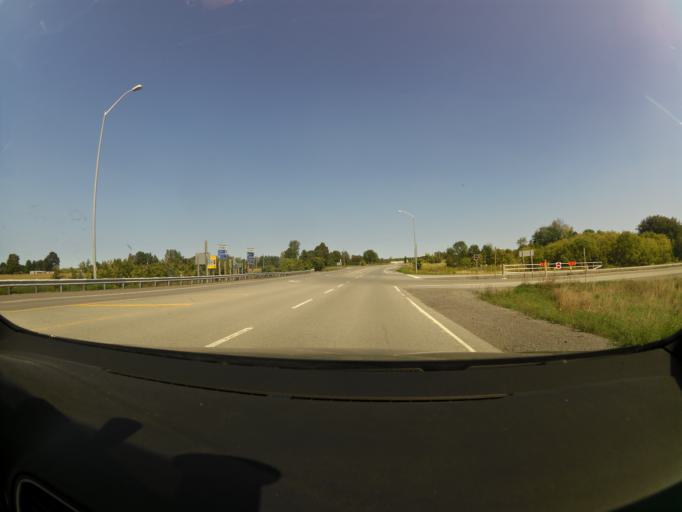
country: CA
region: Ontario
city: Arnprior
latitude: 45.4206
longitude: -76.3269
